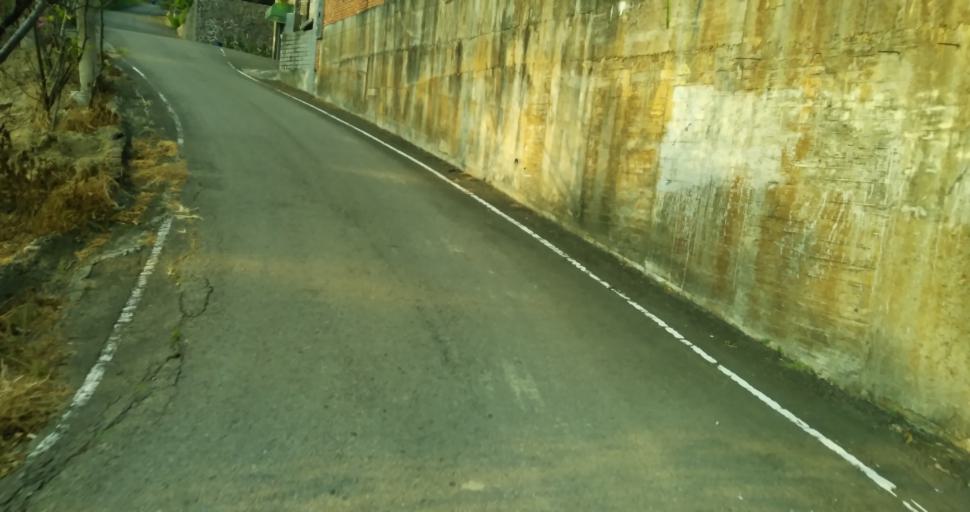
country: TW
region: Taiwan
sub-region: Hsinchu
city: Hsinchu
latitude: 24.7637
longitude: 120.9652
